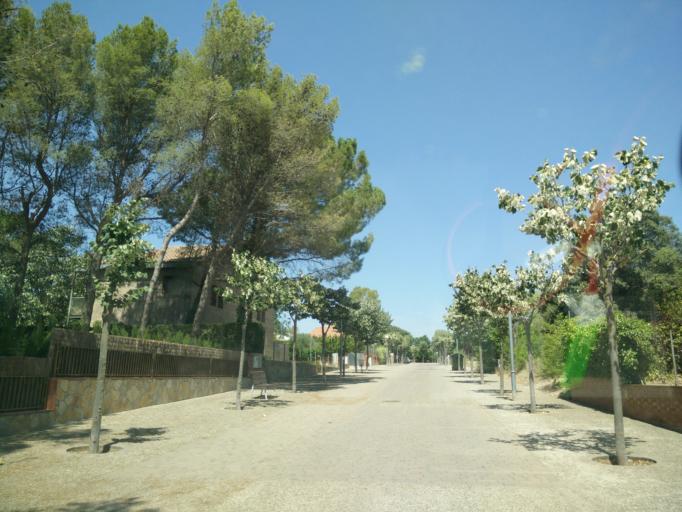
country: ES
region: Catalonia
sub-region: Provincia de Barcelona
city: Piera
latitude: 41.5391
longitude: 1.7650
